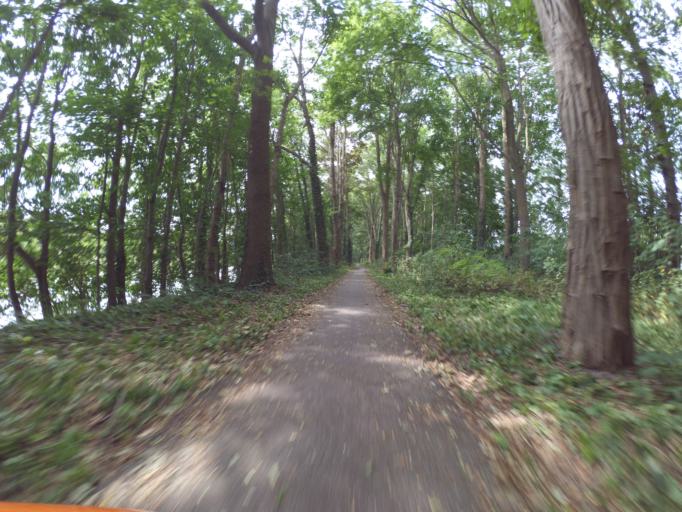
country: NL
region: Overijssel
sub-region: Gemeente Hof van Twente
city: Markelo
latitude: 52.1820
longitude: 6.4748
